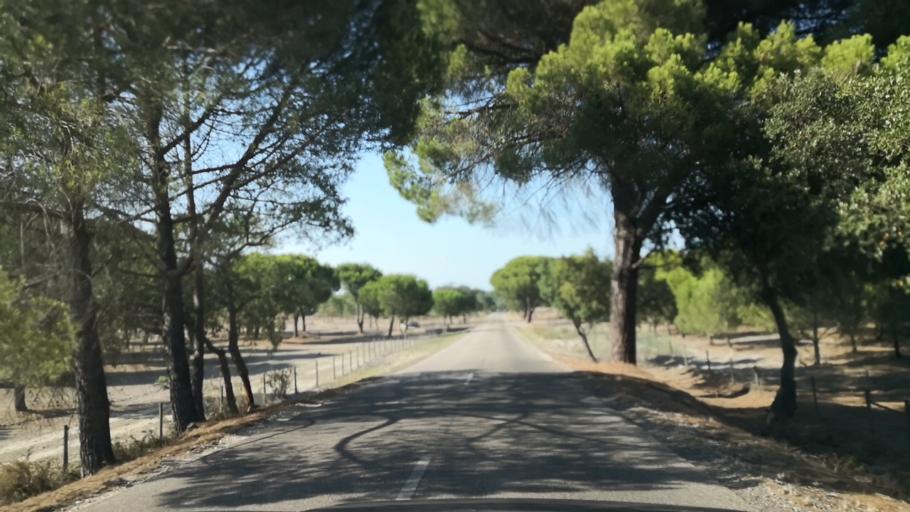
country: PT
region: Santarem
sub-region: Coruche
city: Coruche
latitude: 38.8539
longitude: -8.5450
